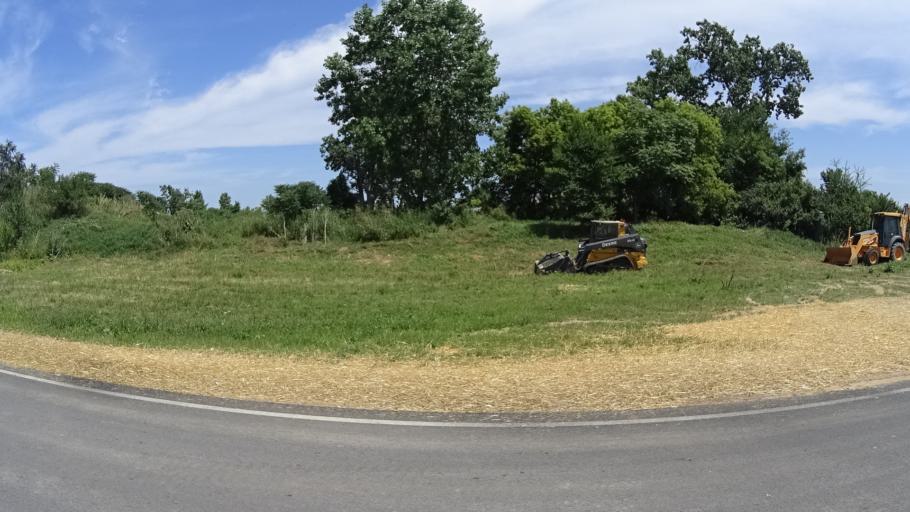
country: US
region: Ohio
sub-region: Erie County
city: Sandusky
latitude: 41.4145
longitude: -82.7717
